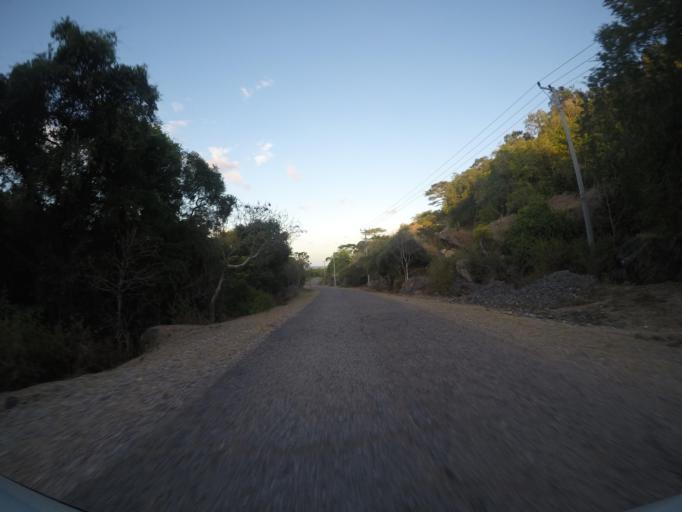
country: TL
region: Lautem
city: Lospalos
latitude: -8.3435
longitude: 127.0359
